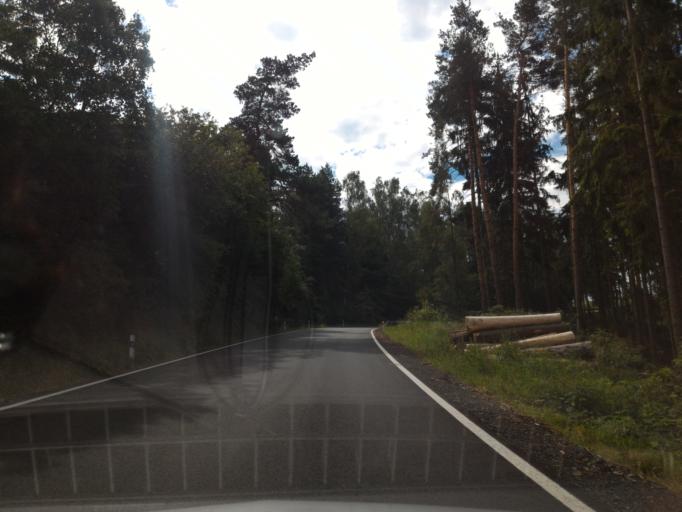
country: CZ
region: Vysocina
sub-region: Okres Jihlava
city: Telc
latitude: 49.1449
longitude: 15.5463
